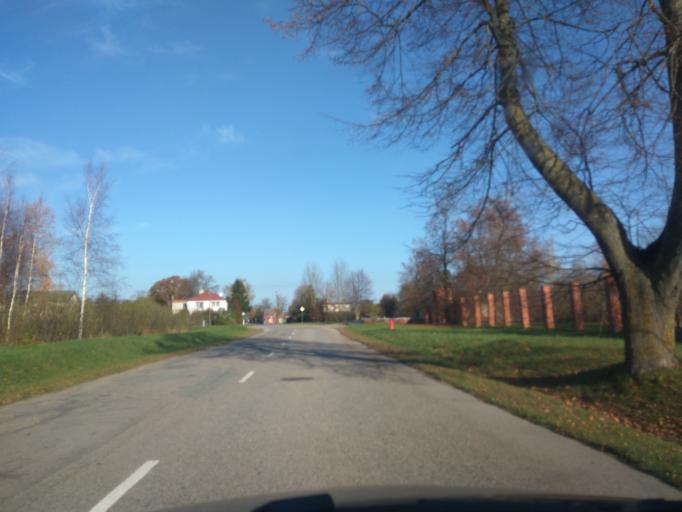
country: LV
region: Ventspils
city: Ventspils
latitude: 57.3703
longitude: 21.5677
